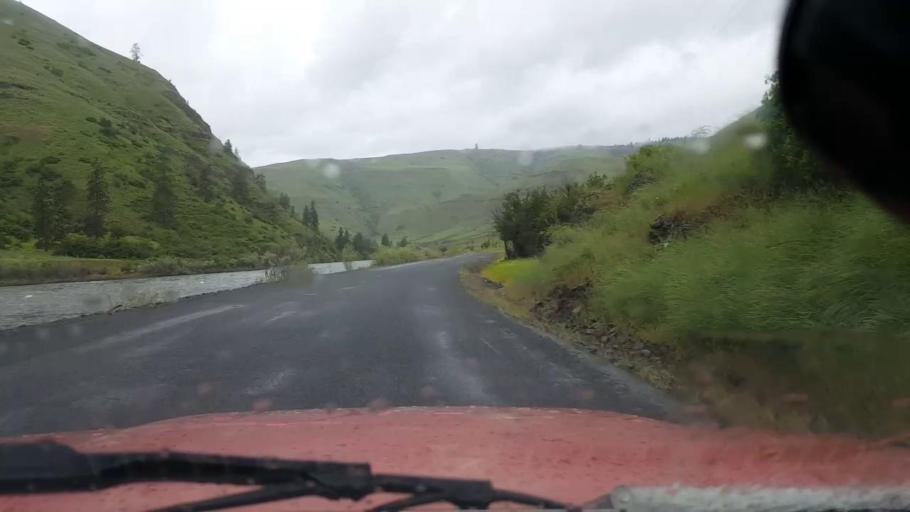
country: US
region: Washington
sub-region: Asotin County
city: Asotin
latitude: 46.0358
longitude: -117.2775
